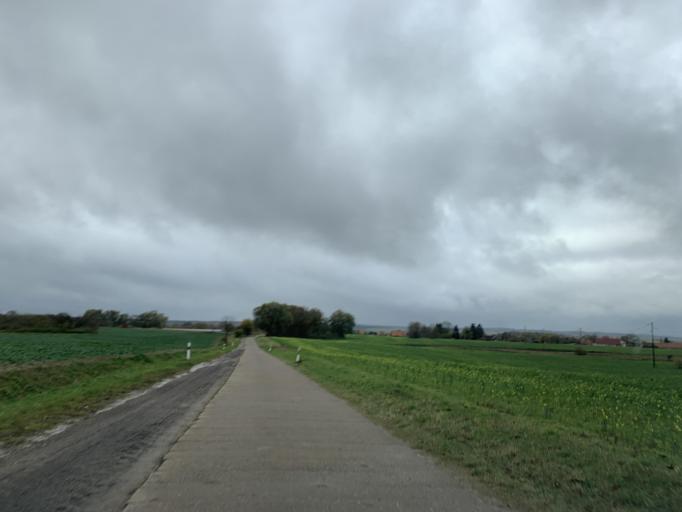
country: DE
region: Mecklenburg-Vorpommern
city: Blankensee
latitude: 53.3801
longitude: 13.2710
